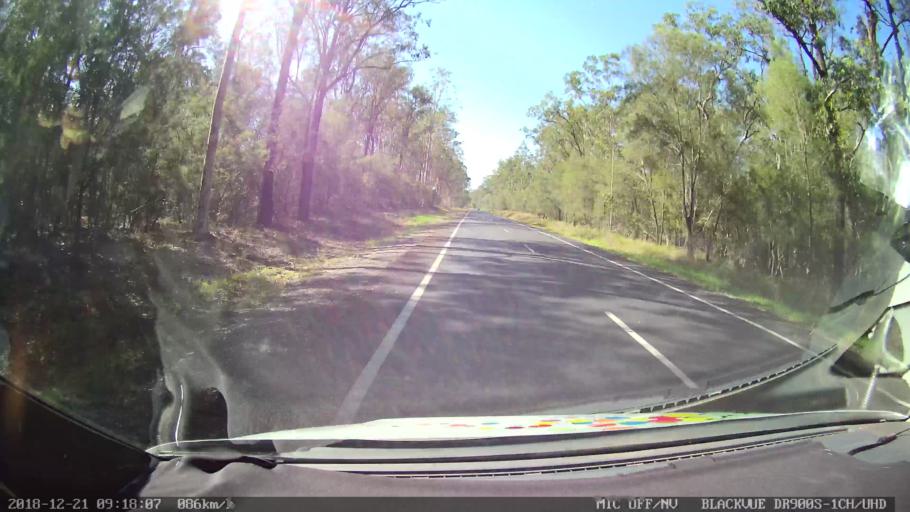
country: AU
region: New South Wales
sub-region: Clarence Valley
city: Maclean
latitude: -29.3005
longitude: 152.9930
